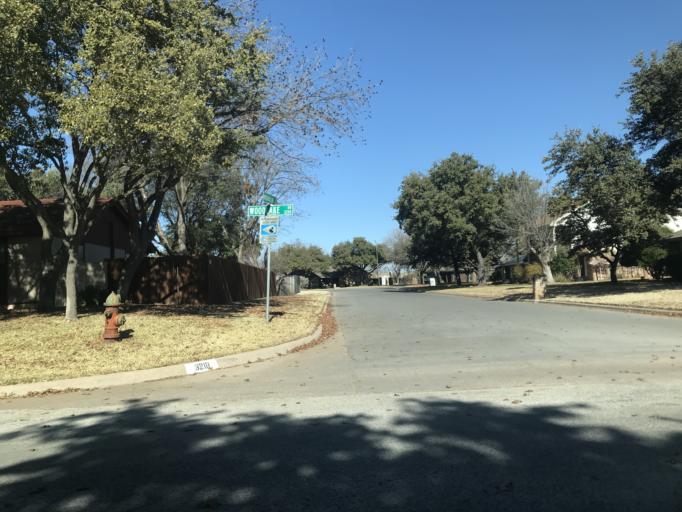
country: US
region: Texas
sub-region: Taylor County
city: Abilene
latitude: 32.3828
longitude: -99.7659
